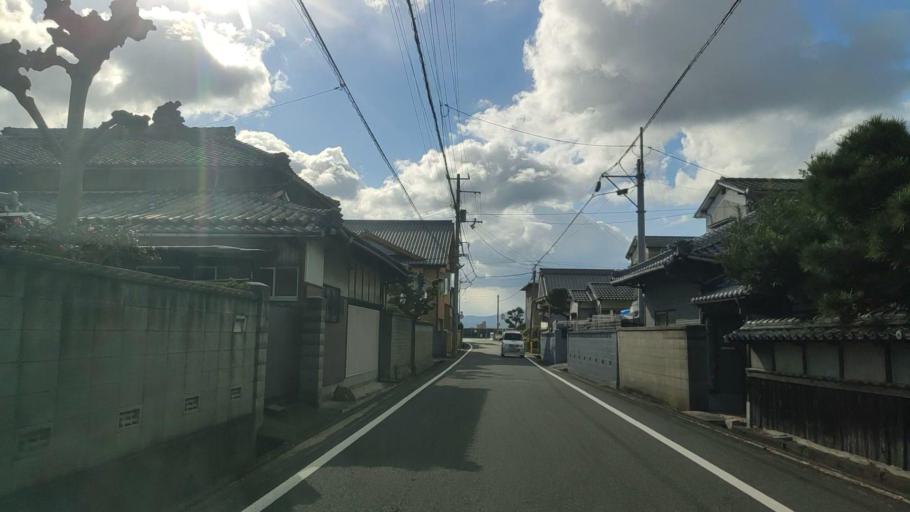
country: JP
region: Ehime
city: Masaki-cho
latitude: 33.8251
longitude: 132.7085
